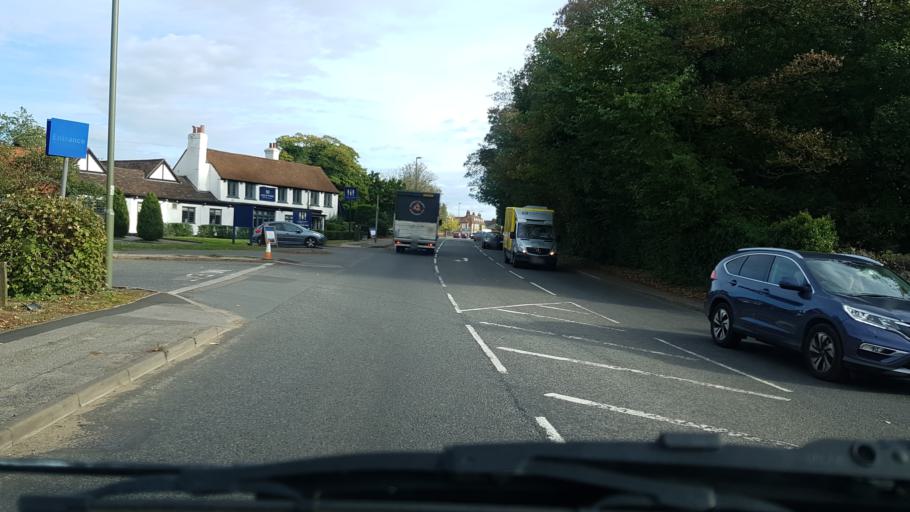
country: GB
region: England
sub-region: Surrey
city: Cobham
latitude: 51.3334
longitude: -0.4224
